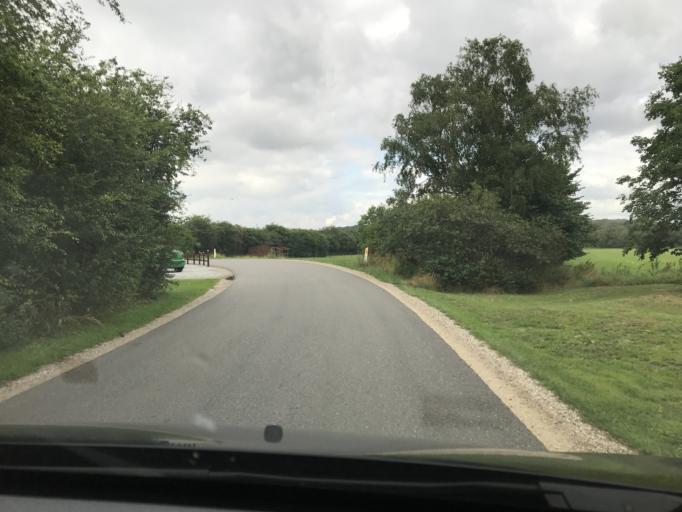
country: DK
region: Central Jutland
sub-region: Syddjurs Kommune
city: Ryomgard
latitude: 56.3765
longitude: 10.4335
